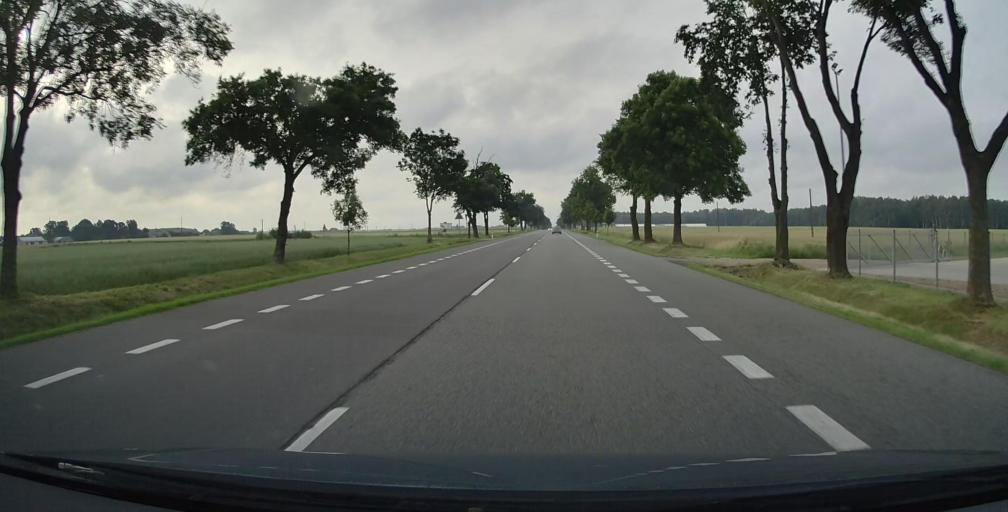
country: PL
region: Masovian Voivodeship
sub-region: Powiat siedlecki
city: Zbuczyn
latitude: 52.1030
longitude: 22.3991
